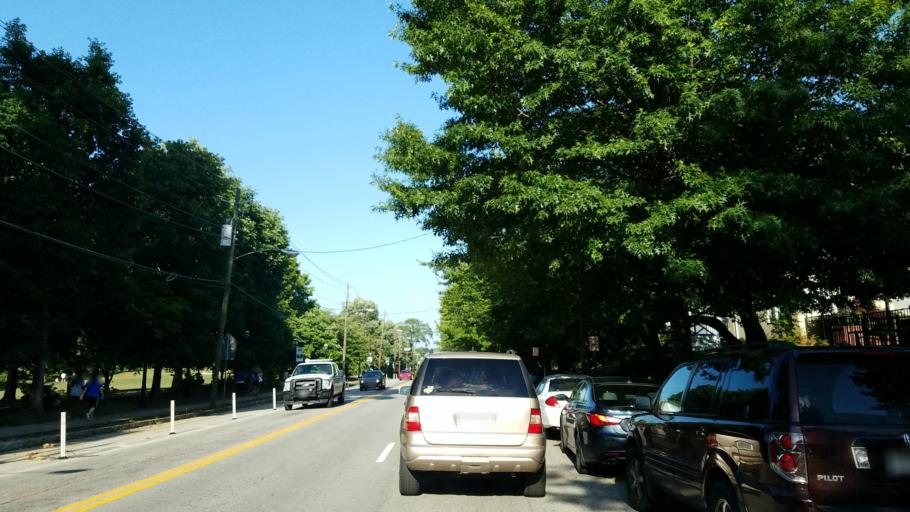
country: US
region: Georgia
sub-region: Fulton County
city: Atlanta
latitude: 33.7817
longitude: -84.3764
